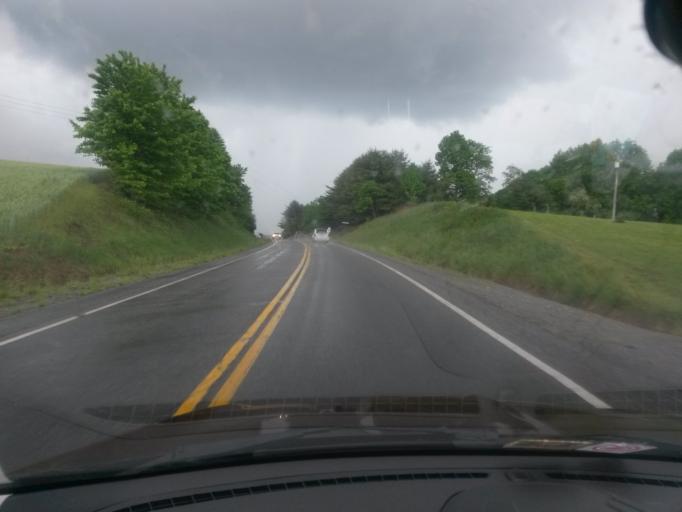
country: US
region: Virginia
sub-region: Floyd County
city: Floyd
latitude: 36.9697
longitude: -80.3855
